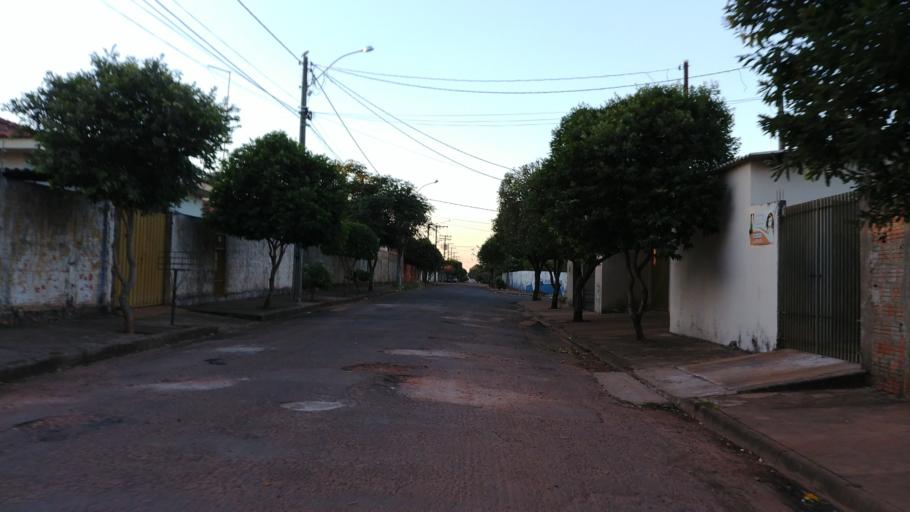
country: BR
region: Sao Paulo
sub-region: Paraguacu Paulista
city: Paraguacu Paulista
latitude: -22.4299
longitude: -50.5740
